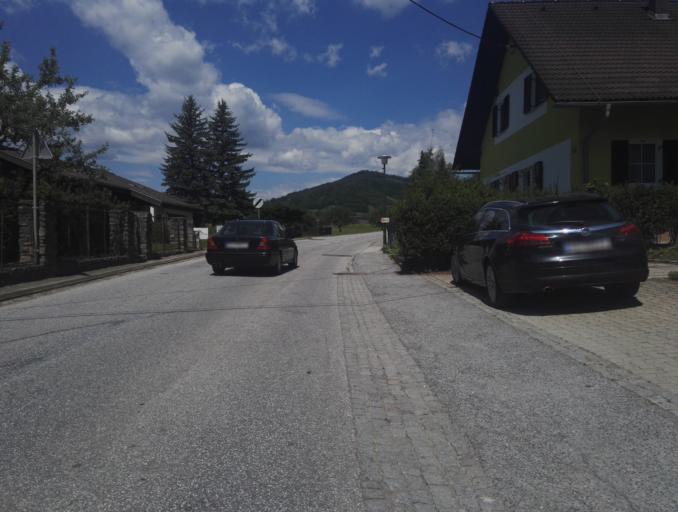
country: AT
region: Styria
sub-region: Politischer Bezirk Graz-Umgebung
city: Peggau
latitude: 47.2004
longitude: 15.3335
